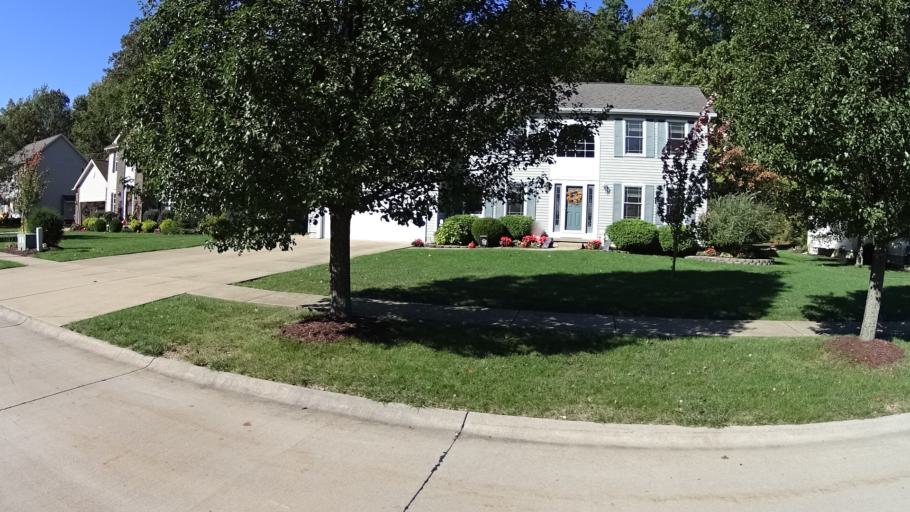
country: US
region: Ohio
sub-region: Lorain County
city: Amherst
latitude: 41.4077
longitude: -82.2499
